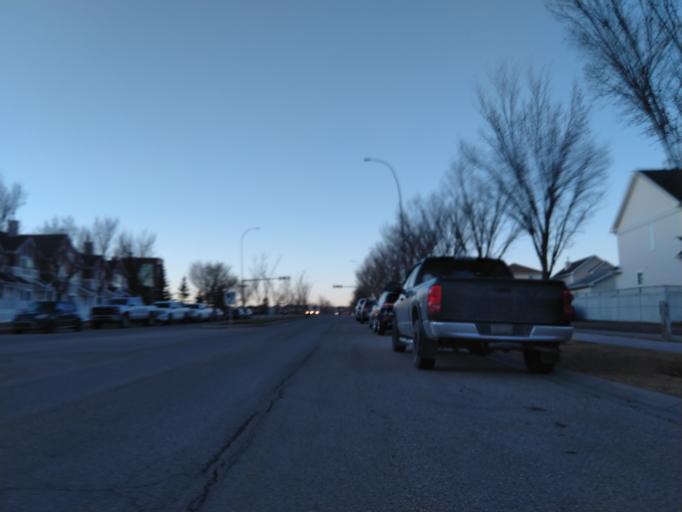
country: CA
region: Alberta
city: Calgary
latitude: 51.1260
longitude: -114.2476
